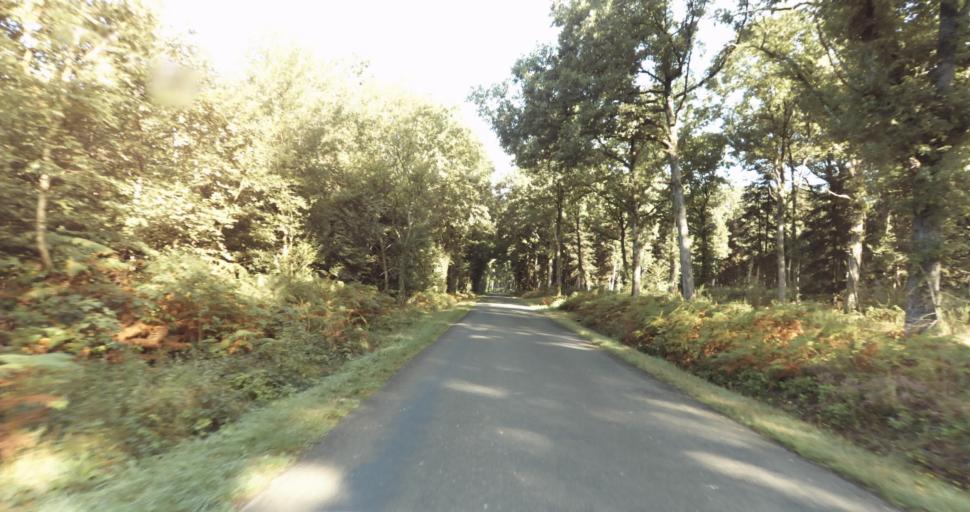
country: FR
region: Lower Normandy
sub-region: Departement de l'Orne
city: Vimoutiers
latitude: 48.9321
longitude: 0.2813
